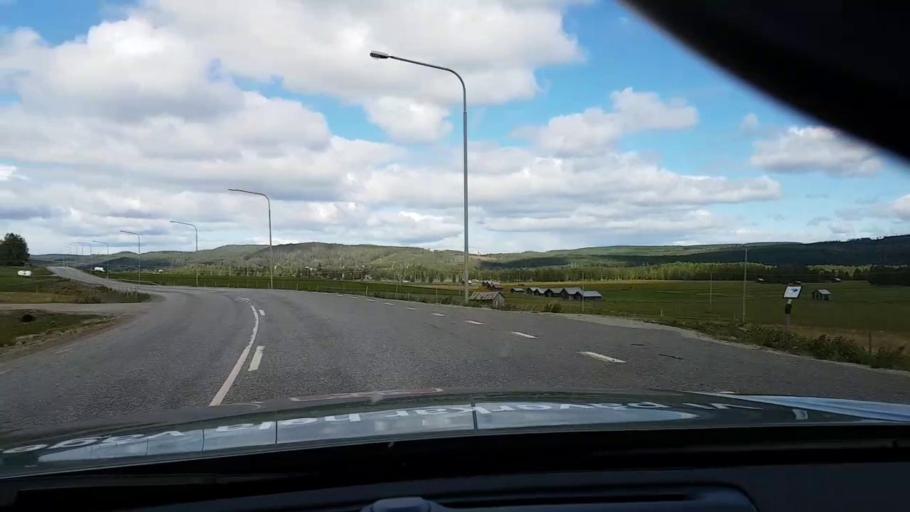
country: SE
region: Vaesternorrland
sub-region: OErnskoeldsviks Kommun
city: Bredbyn
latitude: 63.4978
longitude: 18.0830
